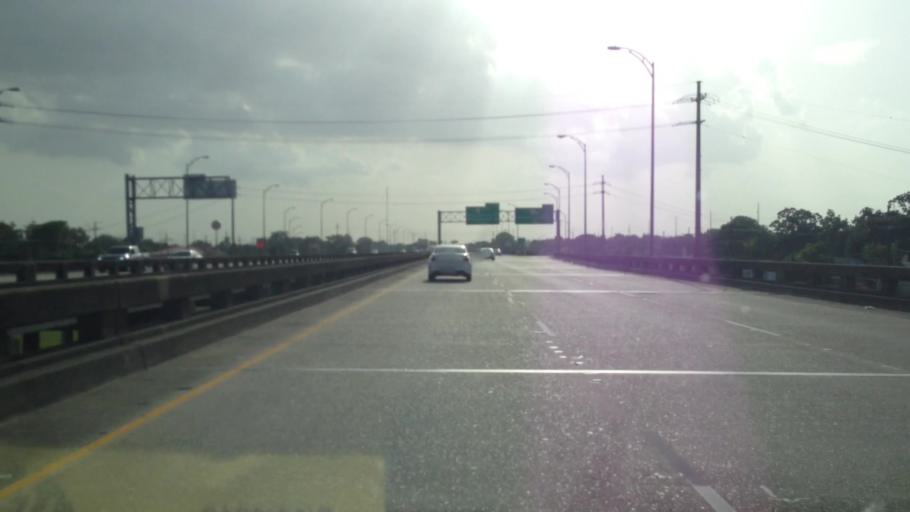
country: US
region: Louisiana
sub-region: Orleans Parish
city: New Orleans
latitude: 29.9917
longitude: -90.0542
